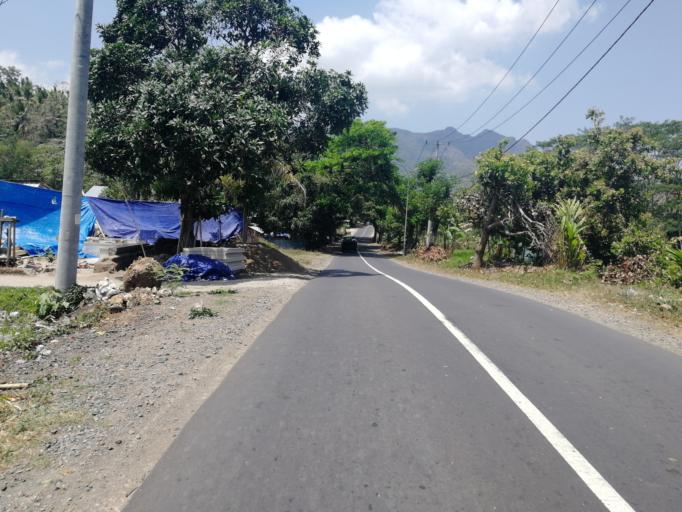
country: ID
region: West Nusa Tenggara
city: Karangsubagan
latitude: -8.4356
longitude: 116.0874
